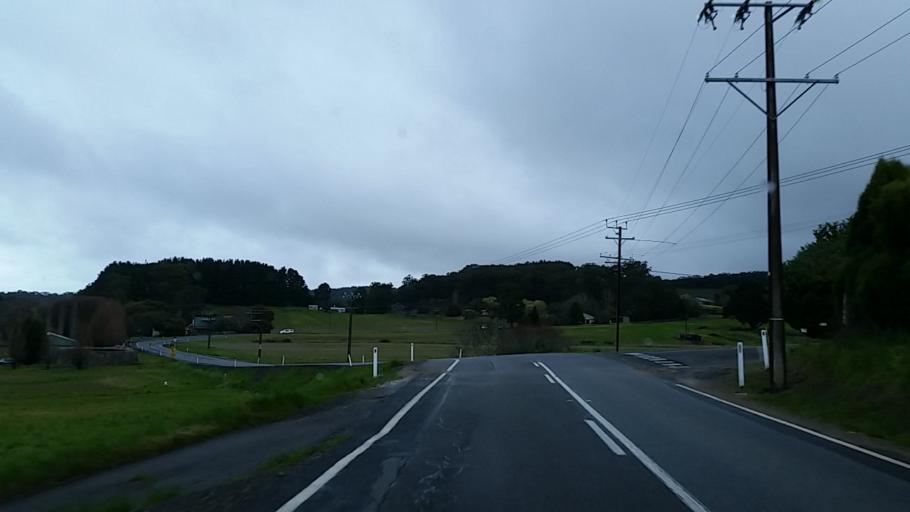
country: AU
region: South Australia
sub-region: Adelaide Hills
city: Bridgewater
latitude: -34.9695
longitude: 138.7334
